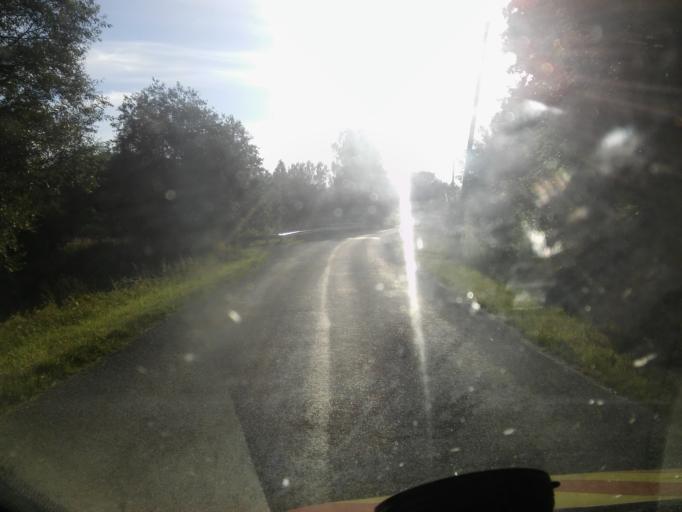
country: EE
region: Valgamaa
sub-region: Torva linn
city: Torva
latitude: 58.0802
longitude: 25.9734
